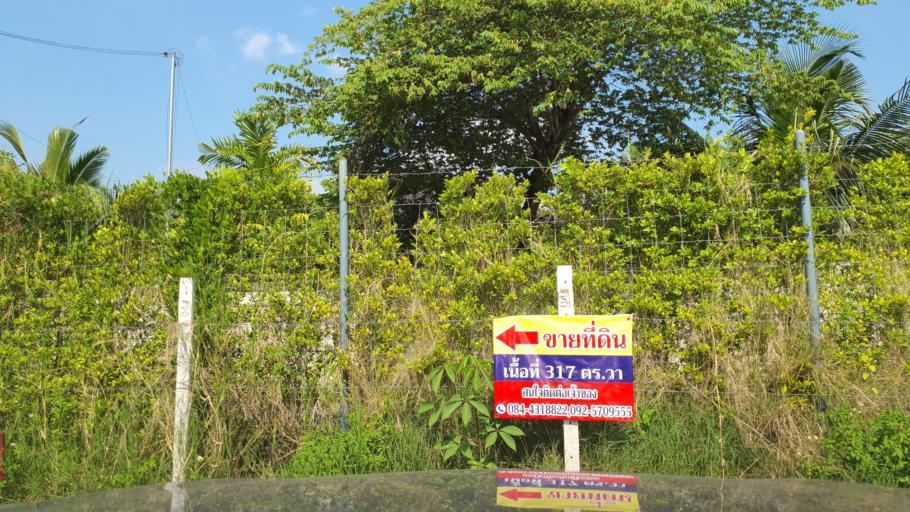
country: TH
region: Chiang Mai
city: Hang Dong
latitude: 18.7107
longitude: 98.9175
